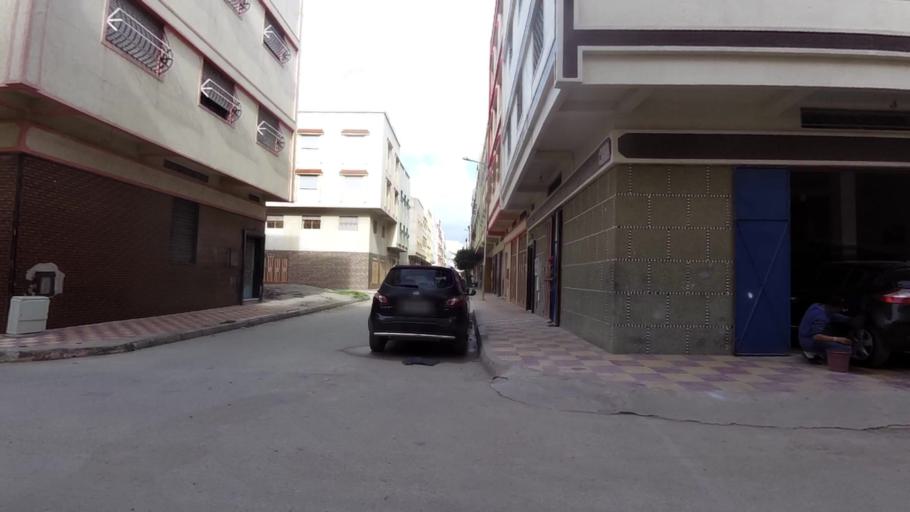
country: MA
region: Tanger-Tetouan
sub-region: Tanger-Assilah
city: Tangier
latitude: 35.7517
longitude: -5.7975
